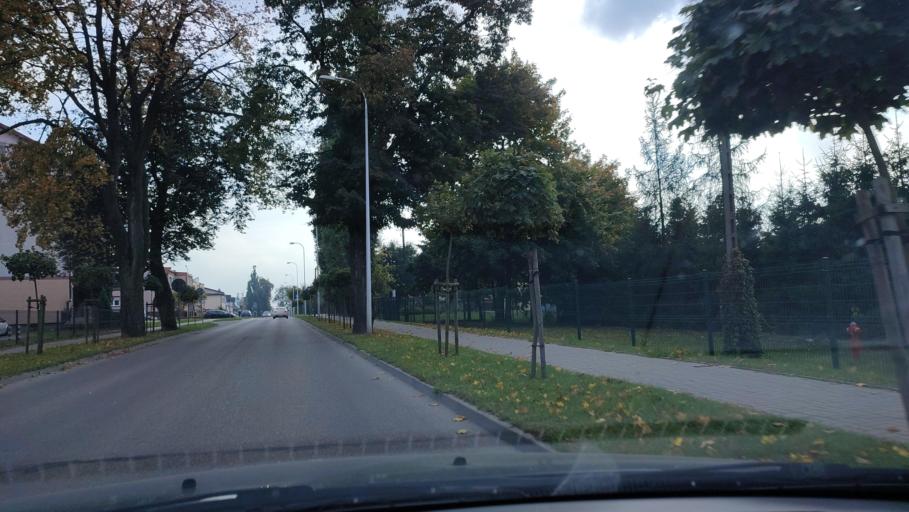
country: PL
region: Warmian-Masurian Voivodeship
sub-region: Powiat dzialdowski
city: Dzialdowo
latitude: 53.2444
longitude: 20.1886
